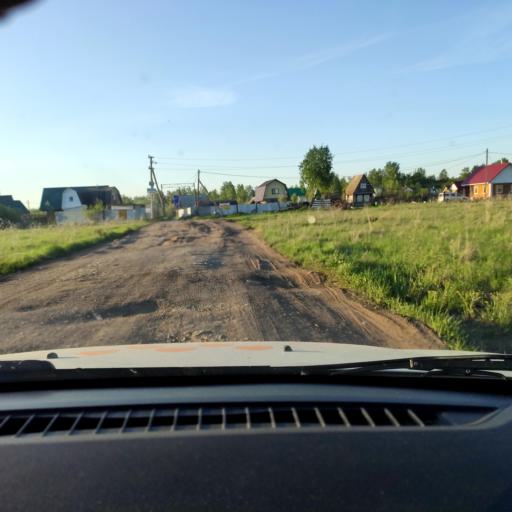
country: RU
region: Bashkortostan
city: Asanovo
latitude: 54.9073
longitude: 55.6178
